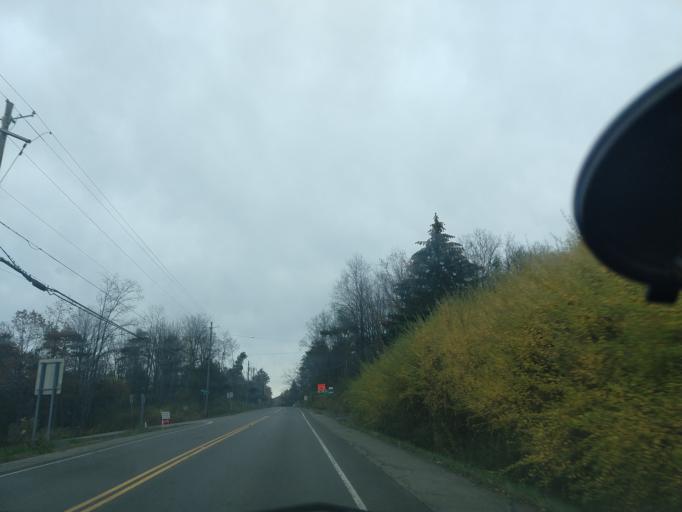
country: US
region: New York
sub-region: Tompkins County
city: East Ithaca
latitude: 42.4333
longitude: -76.4491
